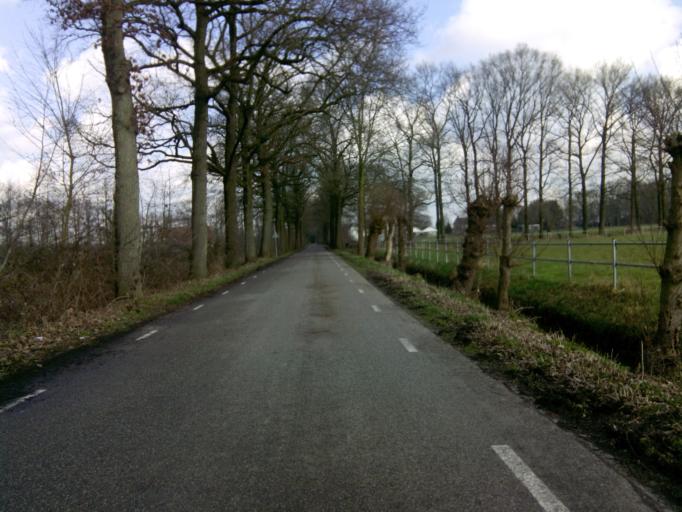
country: NL
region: Utrecht
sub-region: Gemeente Woudenberg
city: Woudenberg
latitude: 52.0854
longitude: 5.4235
